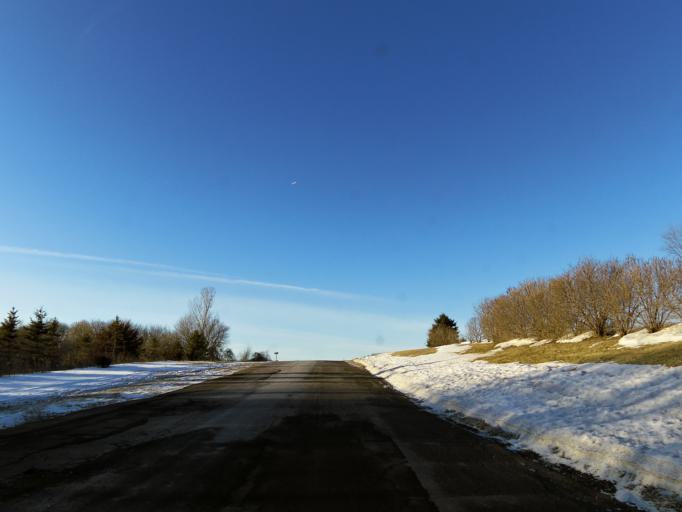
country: US
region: Minnesota
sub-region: Dakota County
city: Hastings
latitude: 44.7965
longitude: -92.8666
